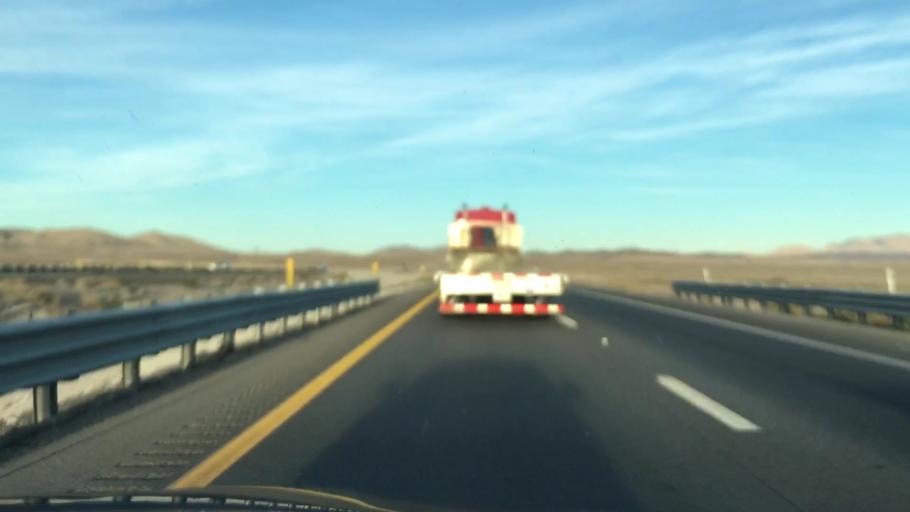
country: US
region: Nevada
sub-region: Clark County
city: Nellis Air Force Base
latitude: 36.2960
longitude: -114.9893
